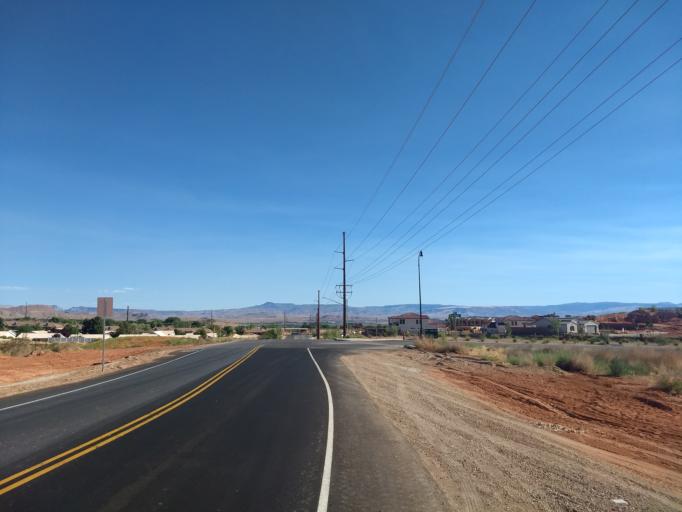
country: US
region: Utah
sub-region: Washington County
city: Washington
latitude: 37.1449
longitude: -113.5098
